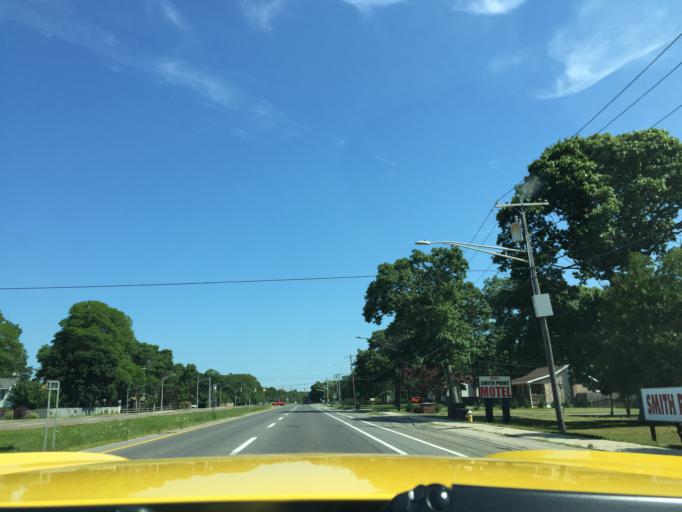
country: US
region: New York
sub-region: Suffolk County
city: Mastic Beach
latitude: 40.7513
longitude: -72.8716
